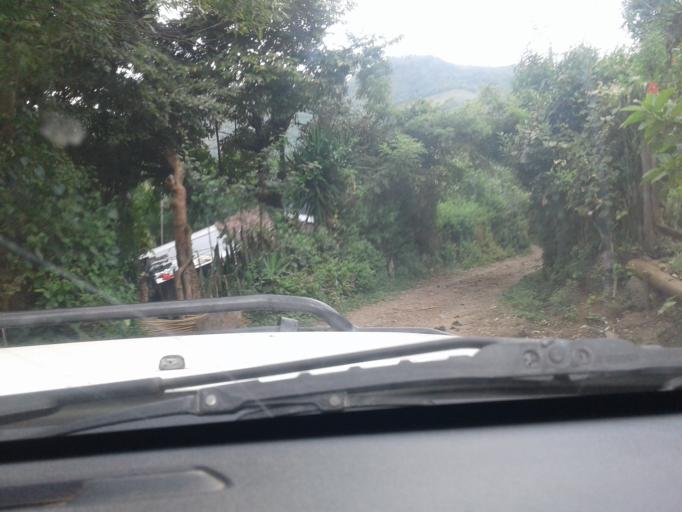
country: NI
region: Matagalpa
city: Terrabona
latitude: 12.7878
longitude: -85.9860
